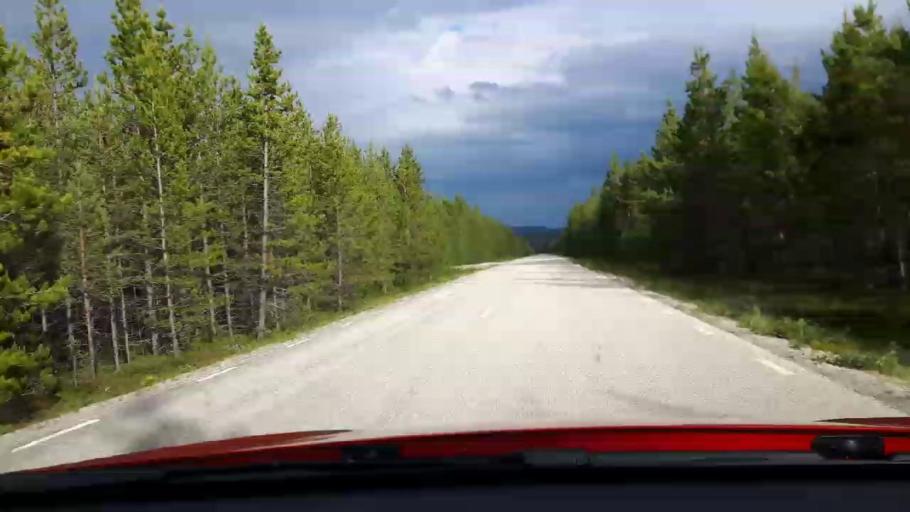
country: SE
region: Jaemtland
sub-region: Bergs Kommun
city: Hoverberg
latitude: 62.6712
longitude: 14.0283
